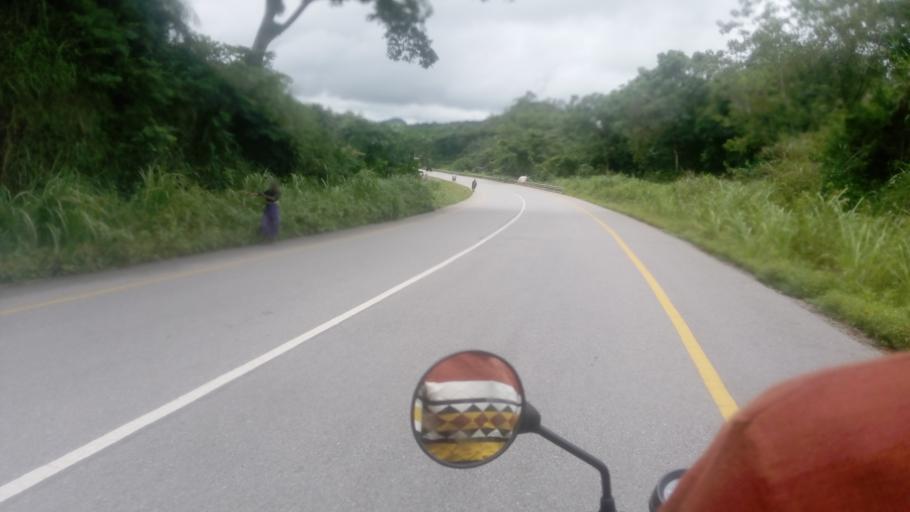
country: SL
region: Northern Province
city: Masaka
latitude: 8.6429
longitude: -11.7401
